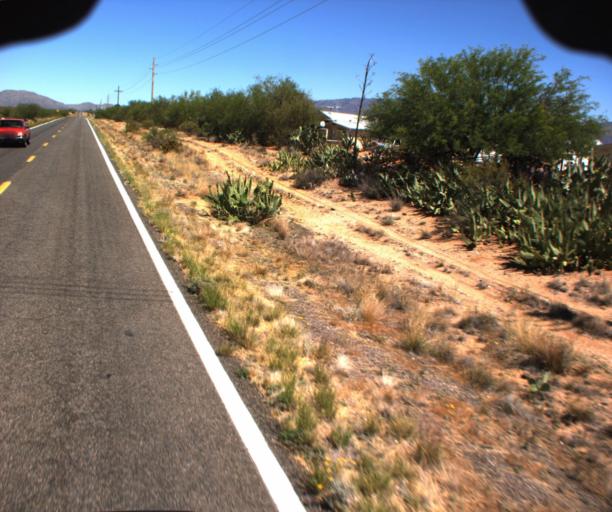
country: US
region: Arizona
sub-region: Yavapai County
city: Congress
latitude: 34.1000
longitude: -112.8300
